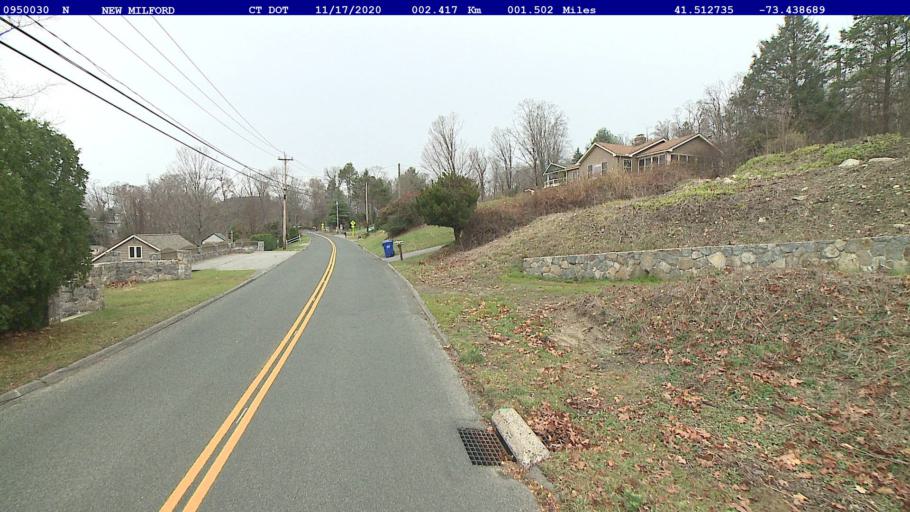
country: US
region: Connecticut
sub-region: Litchfield County
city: New Milford
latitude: 41.5128
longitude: -73.4387
